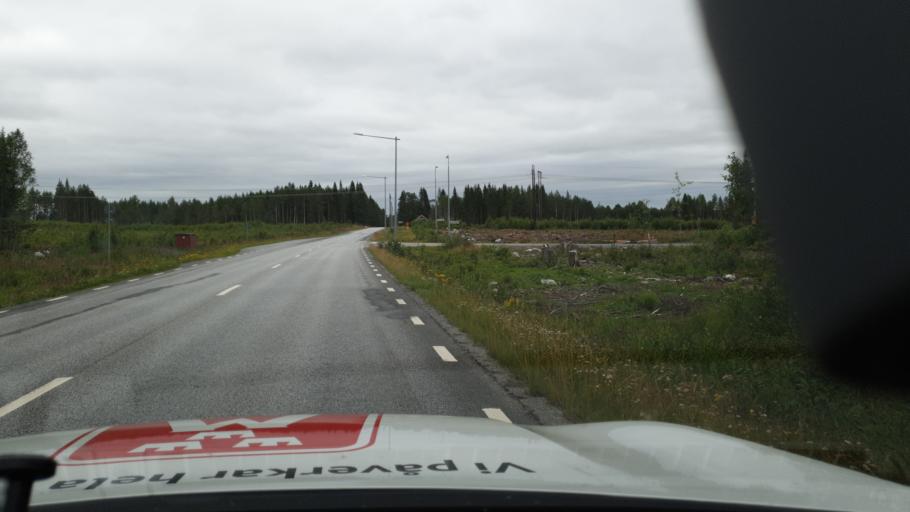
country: SE
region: Vaesterbotten
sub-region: Umea Kommun
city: Ersmark
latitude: 63.8690
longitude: 20.3013
